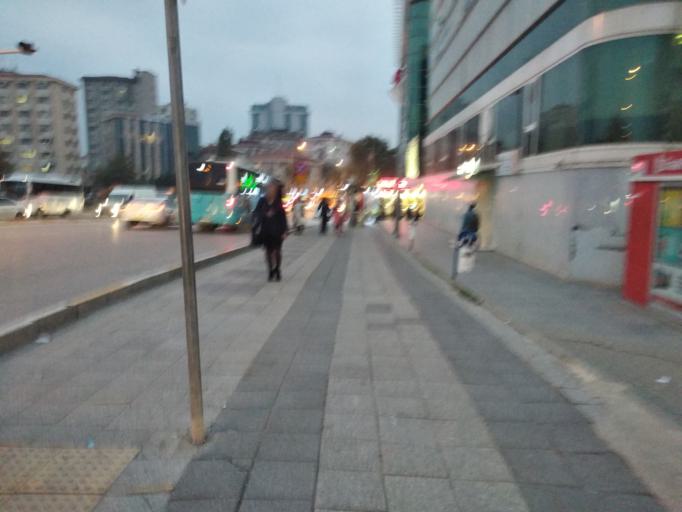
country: TR
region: Istanbul
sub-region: Atasehir
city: Atasehir
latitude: 40.9790
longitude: 29.1251
